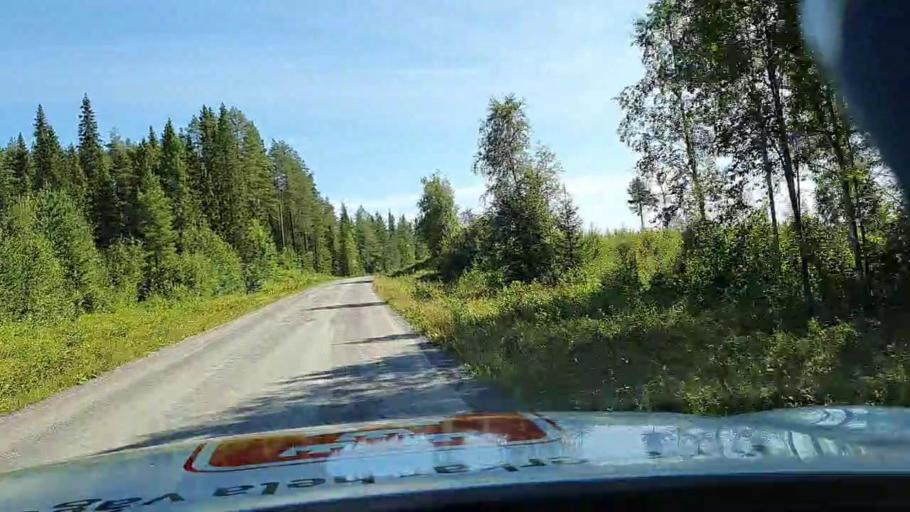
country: SE
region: Jaemtland
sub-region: Krokoms Kommun
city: Krokom
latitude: 63.6849
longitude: 14.5765
